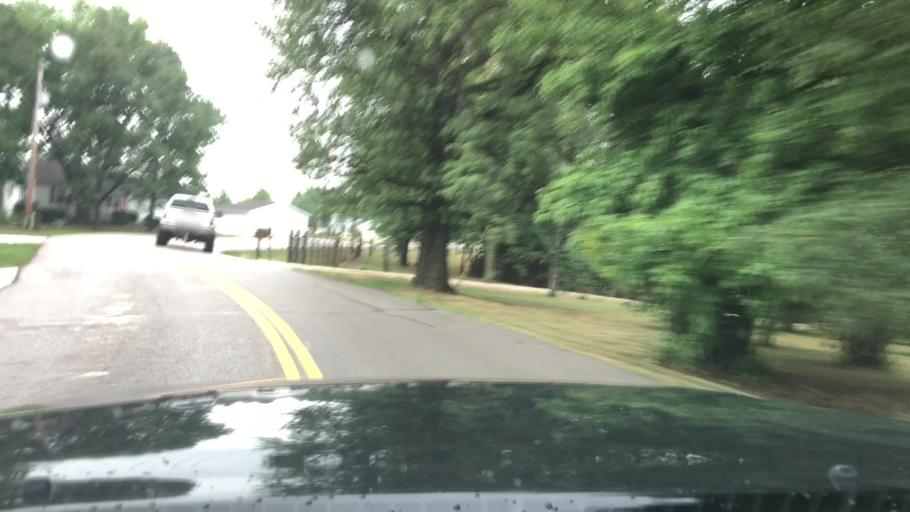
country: US
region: Missouri
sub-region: Saint Charles County
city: Wentzville
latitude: 38.8524
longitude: -90.8760
